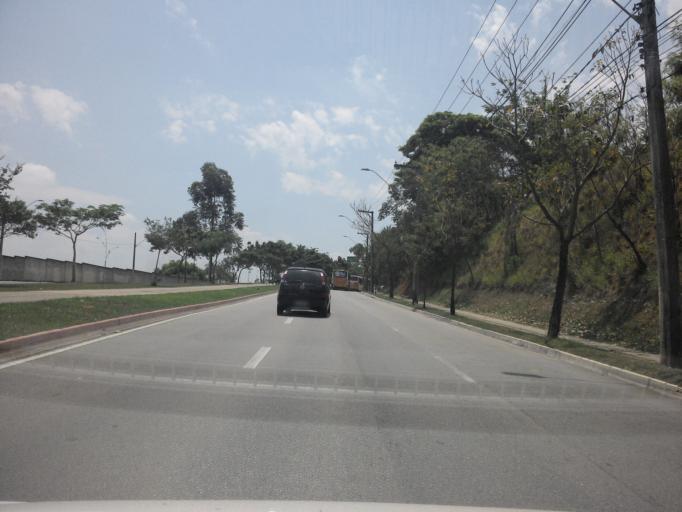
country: BR
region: Sao Paulo
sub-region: Sao Jose Dos Campos
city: Sao Jose dos Campos
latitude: -23.1669
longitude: -45.8077
